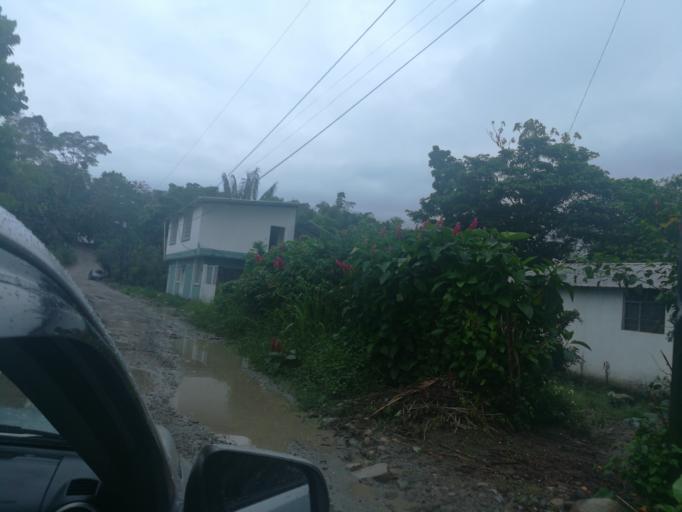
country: EC
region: Napo
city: Tena
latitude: -1.0379
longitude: -77.6621
